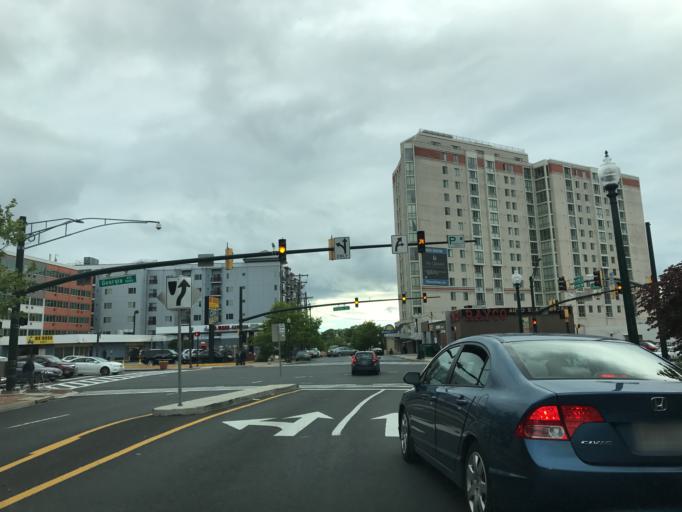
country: US
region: Maryland
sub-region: Montgomery County
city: Silver Spring
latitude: 38.9874
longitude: -77.0261
